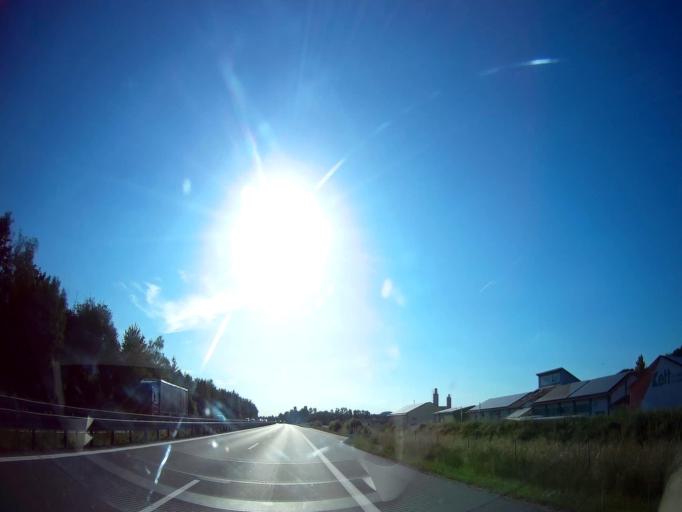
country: DE
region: Bavaria
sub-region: Upper Palatinate
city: Worth an der Donau
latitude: 48.9977
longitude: 12.3898
